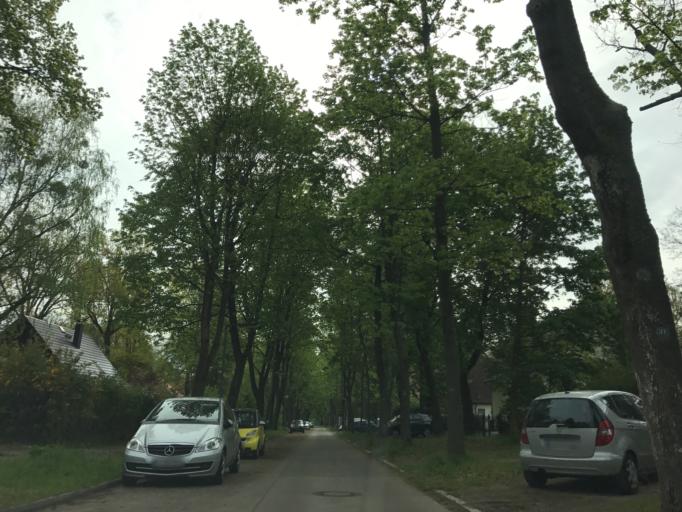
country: DE
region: Berlin
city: Gatow
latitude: 52.4734
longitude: 13.1779
